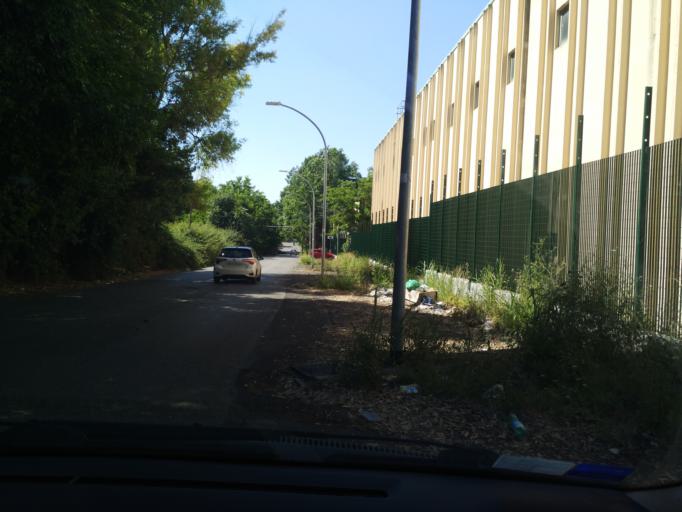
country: IT
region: Latium
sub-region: Citta metropolitana di Roma Capitale
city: Vitinia
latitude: 41.8314
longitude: 12.4560
